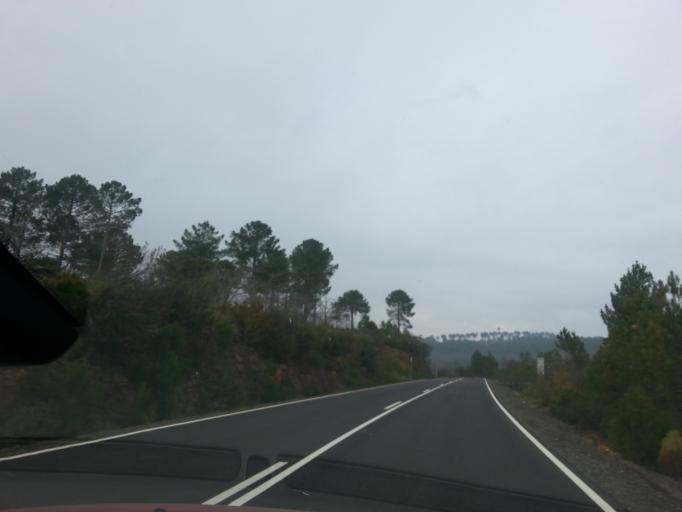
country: ES
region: Castille and Leon
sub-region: Provincia de Salamanca
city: Sotoserrano
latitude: 40.4417
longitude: -6.0479
